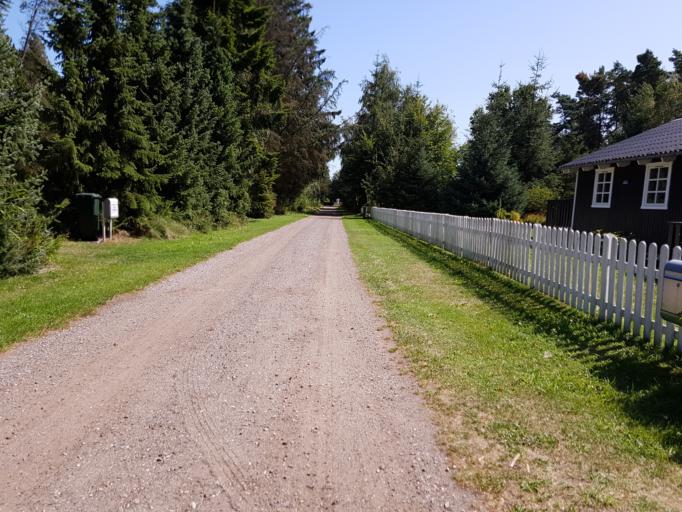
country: DK
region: Zealand
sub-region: Guldborgsund Kommune
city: Nykobing Falster
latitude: 54.6036
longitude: 11.9530
